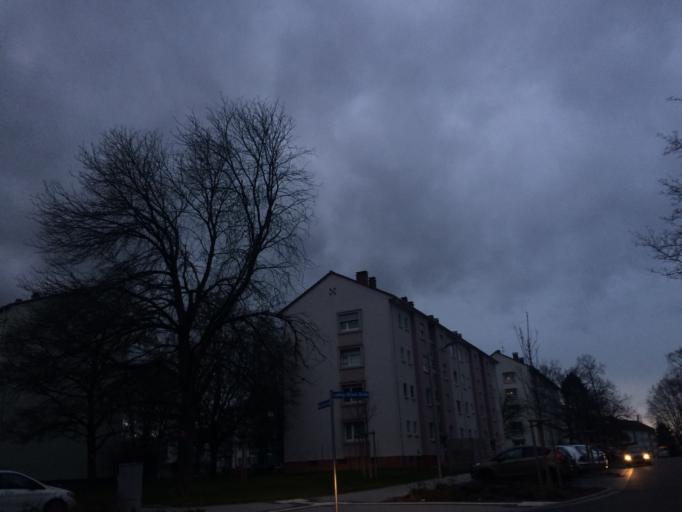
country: DE
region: Rheinland-Pfalz
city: Speyer
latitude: 49.3202
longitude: 8.4154
